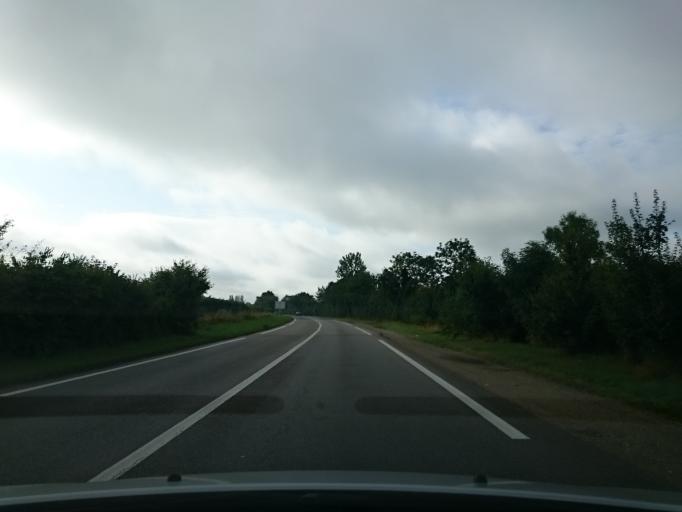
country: FR
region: Lower Normandy
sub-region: Departement du Calvados
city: Cambremer
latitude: 49.1394
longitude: -0.0080
